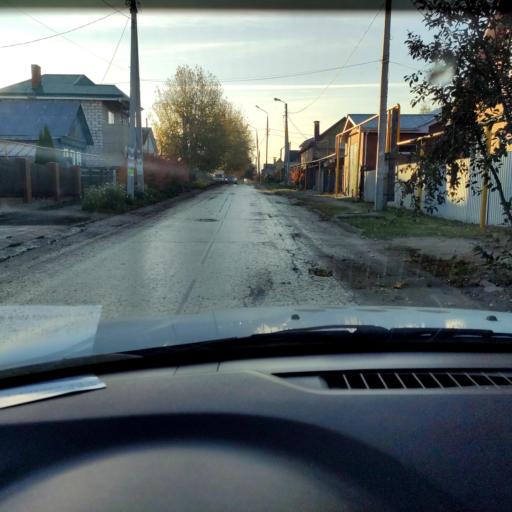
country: RU
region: Samara
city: Tol'yatti
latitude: 53.5253
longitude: 49.4039
